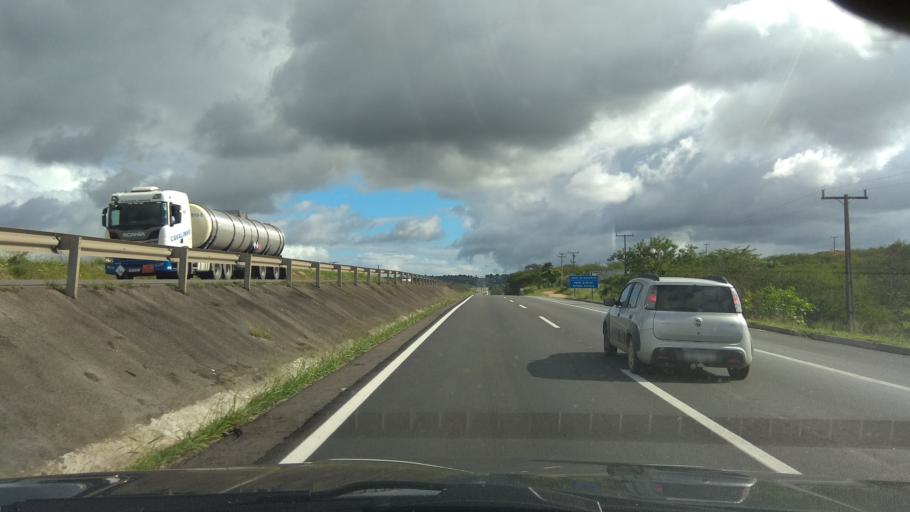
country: BR
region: Bahia
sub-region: Santo Estevao
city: Santo Estevao
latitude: -12.4252
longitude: -39.2086
